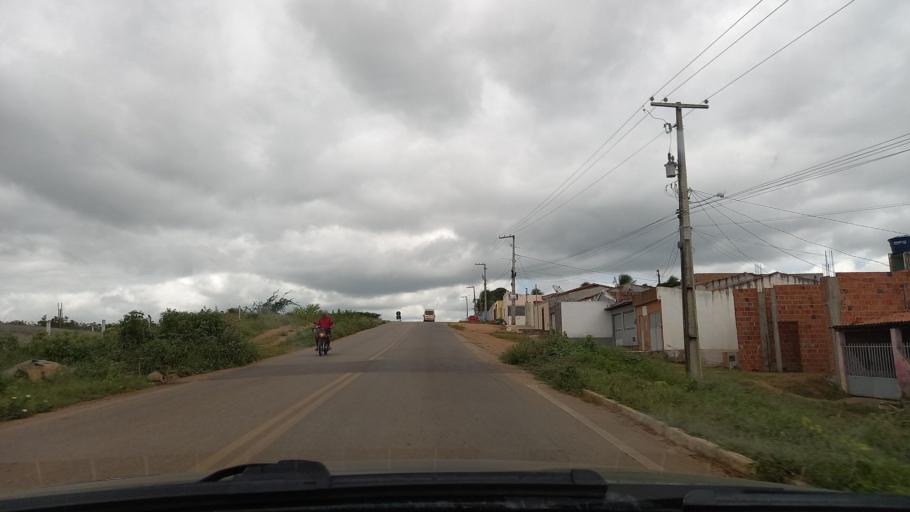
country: BR
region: Sergipe
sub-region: Caninde De Sao Francisco
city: Caninde de Sao Francisco
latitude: -9.6689
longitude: -37.7976
